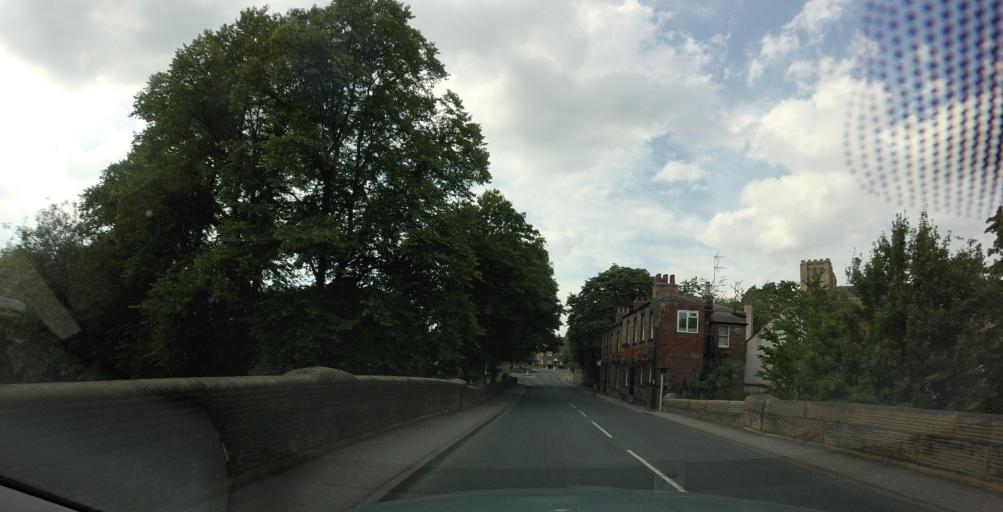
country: GB
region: England
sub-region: North Yorkshire
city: Ripon
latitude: 54.1335
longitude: -1.5205
